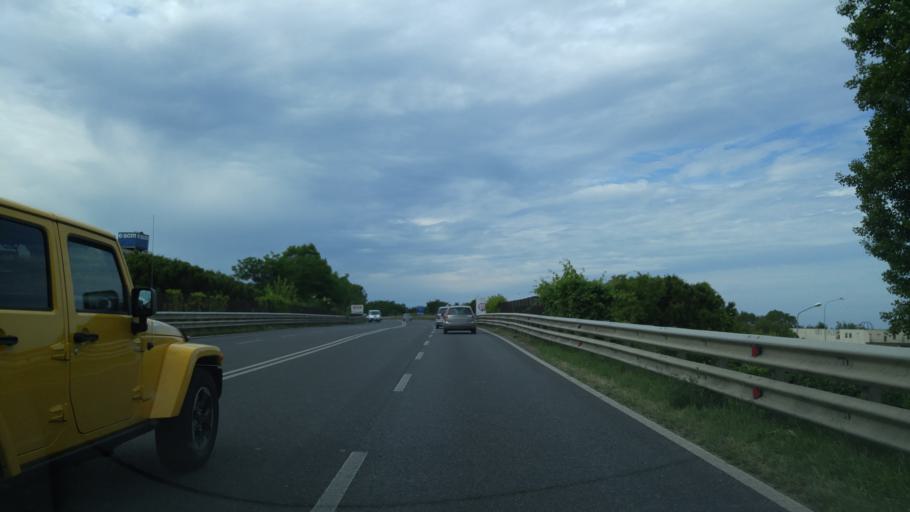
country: IT
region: Emilia-Romagna
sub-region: Provincia di Rimini
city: Rimini
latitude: 44.0682
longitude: 12.5412
